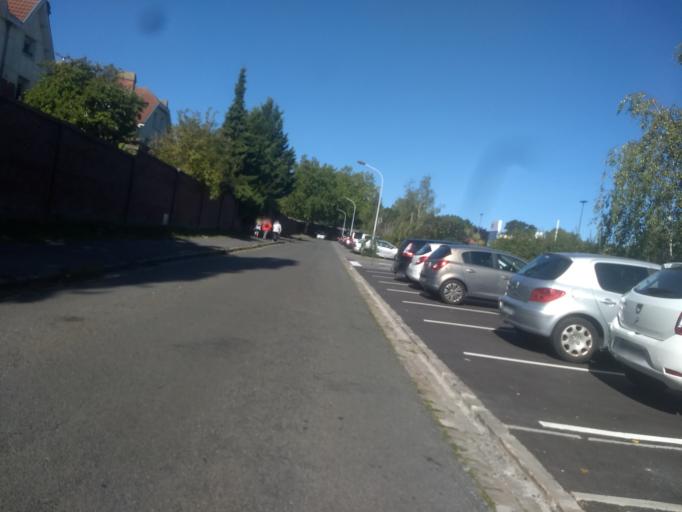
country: FR
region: Nord-Pas-de-Calais
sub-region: Departement du Pas-de-Calais
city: Sainte-Catherine
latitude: 50.2937
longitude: 2.7558
